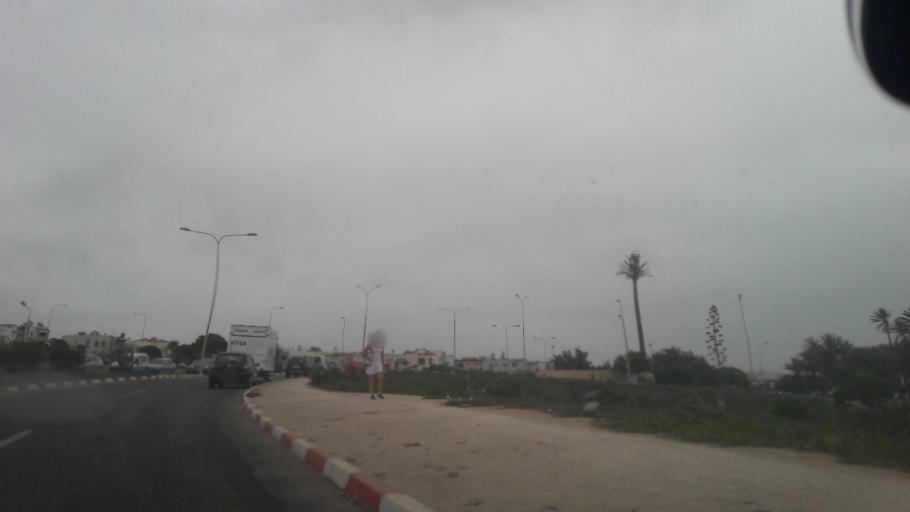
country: MA
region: Souss-Massa-Draa
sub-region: Agadir-Ida-ou-Tnan
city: Agadir
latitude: 30.3967
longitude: -9.5954
